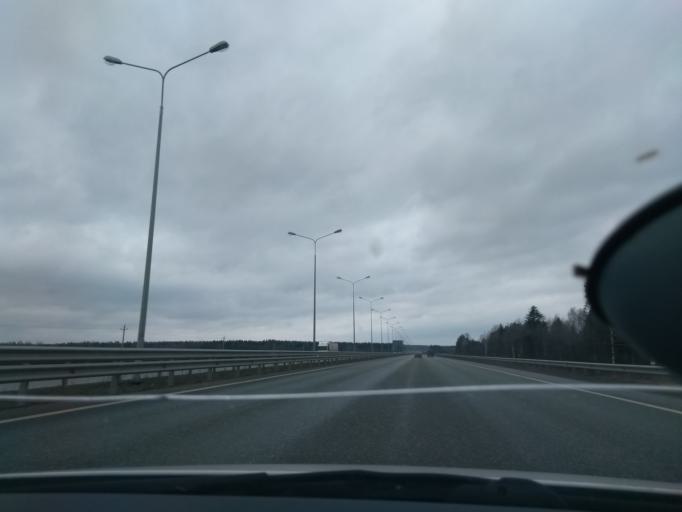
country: RU
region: Perm
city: Bershet'
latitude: 57.6855
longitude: 56.4169
